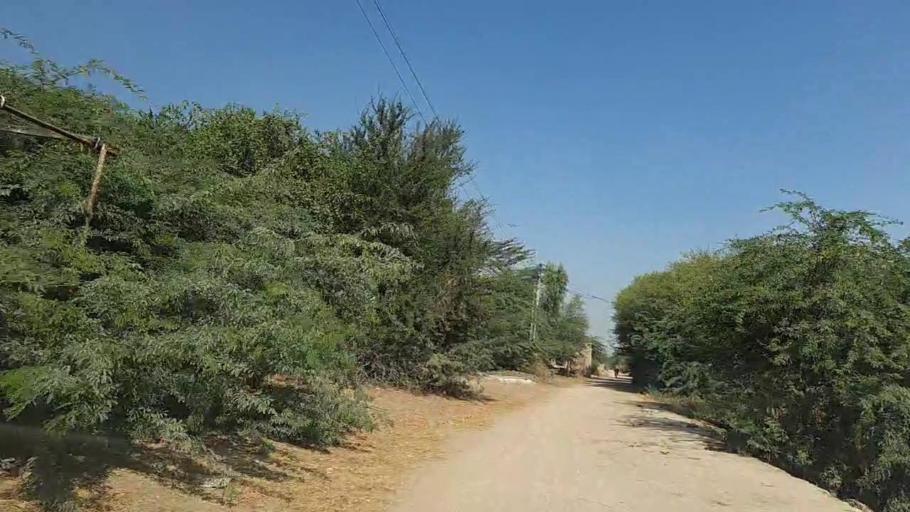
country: PK
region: Sindh
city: Daro Mehar
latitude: 24.7970
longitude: 68.1790
